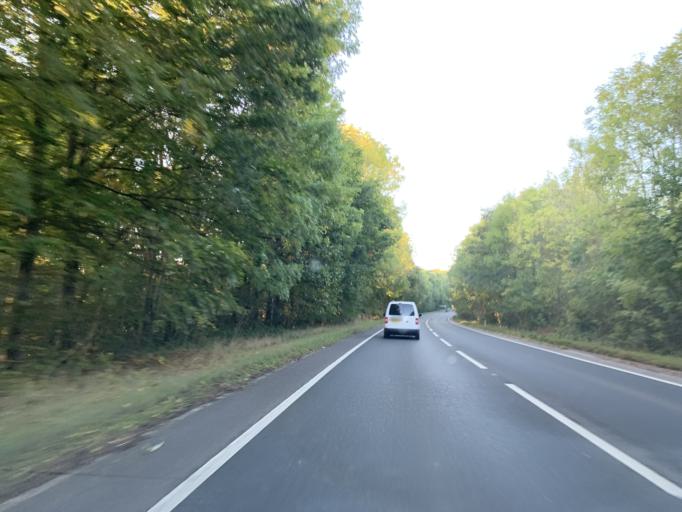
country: GB
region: England
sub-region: Wiltshire
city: Whiteparish
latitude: 50.9841
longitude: -1.6401
